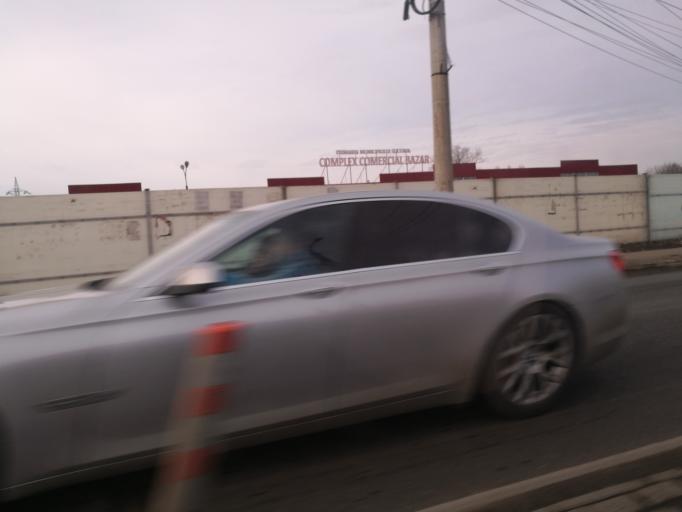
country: RO
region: Suceava
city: Suceava
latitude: 47.6597
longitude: 26.2650
